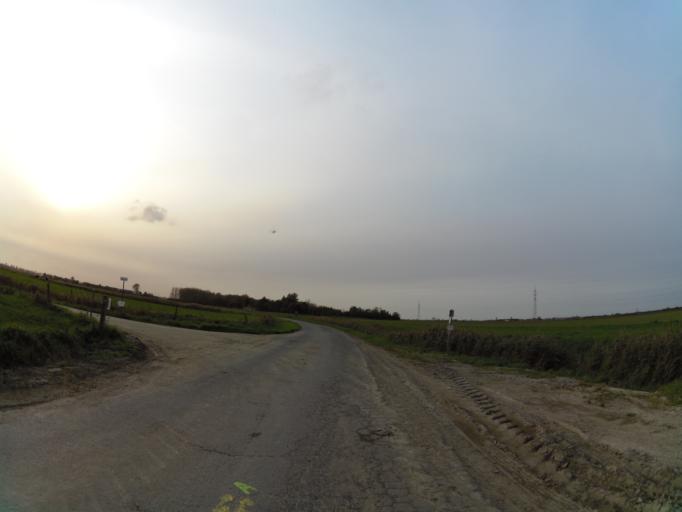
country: BE
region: Flanders
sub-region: Provincie West-Vlaanderen
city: De Haan
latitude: 51.2211
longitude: 3.0418
